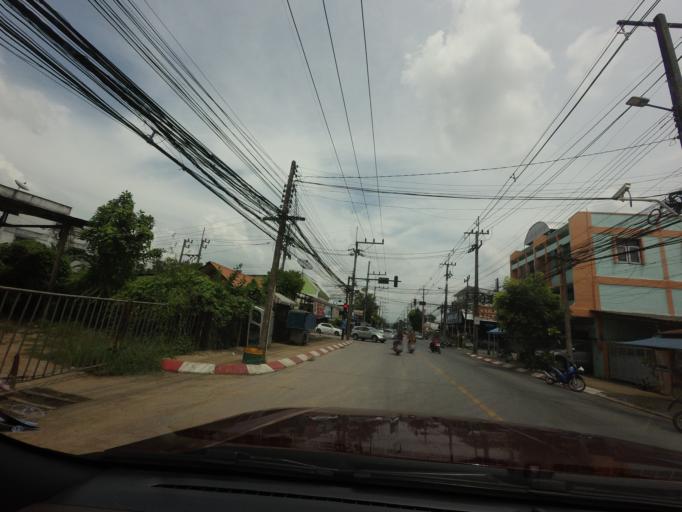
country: TH
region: Yala
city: Yala
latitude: 6.5481
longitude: 101.2931
